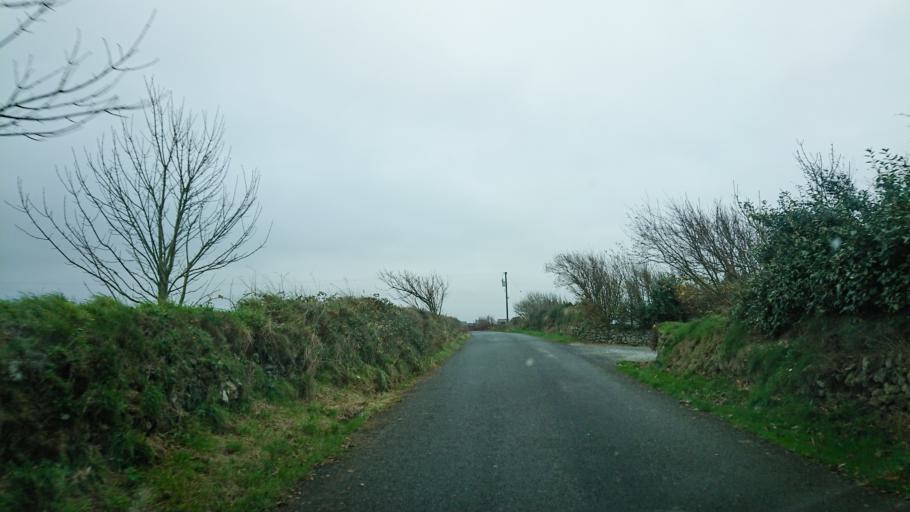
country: IE
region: Munster
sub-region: Waterford
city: Tra Mhor
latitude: 52.1400
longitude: -7.2312
